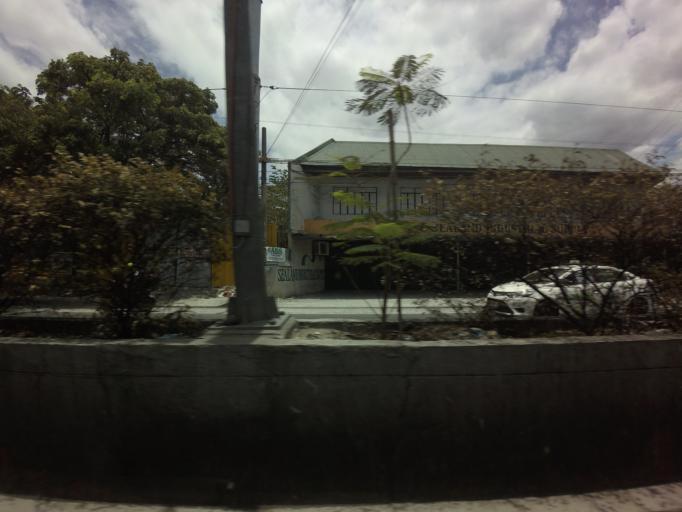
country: PH
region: Metro Manila
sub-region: Marikina
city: Calumpang
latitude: 14.6154
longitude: 121.1021
